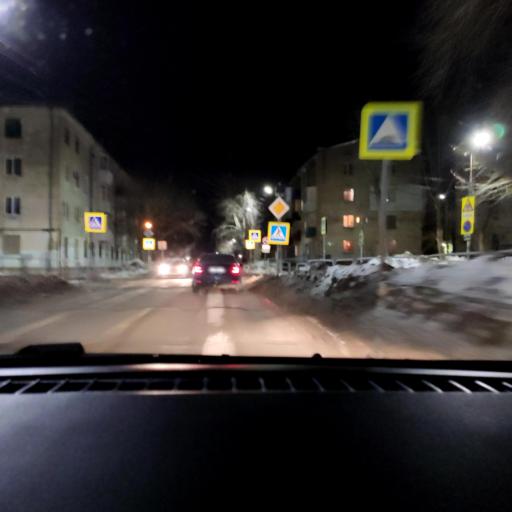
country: RU
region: Samara
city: Novokuybyshevsk
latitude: 53.0943
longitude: 49.9545
